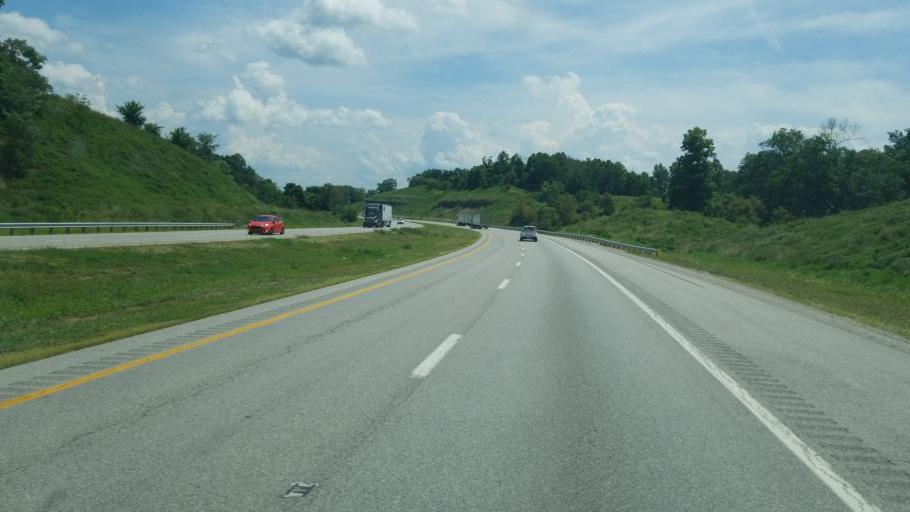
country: US
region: West Virginia
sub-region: Mason County
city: Point Pleasant
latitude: 38.7911
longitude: -82.0944
